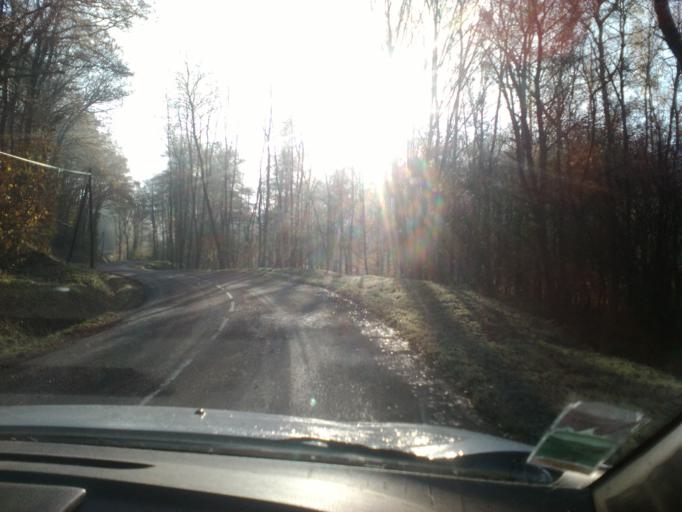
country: FR
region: Lorraine
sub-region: Departement des Vosges
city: Uzemain
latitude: 48.0607
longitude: 6.3385
